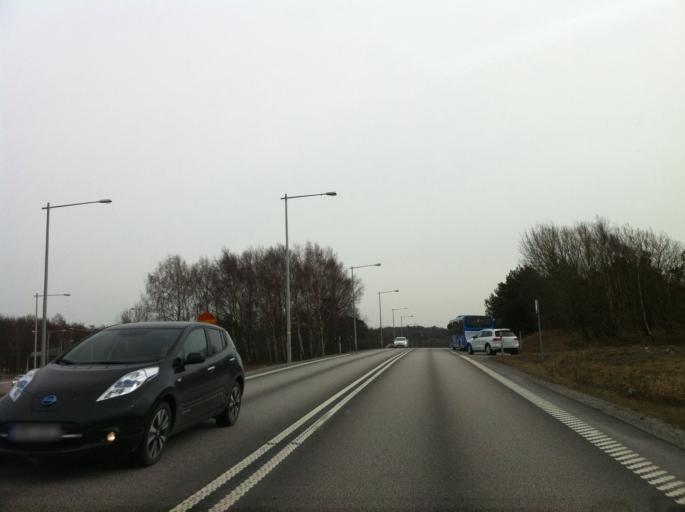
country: SE
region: Vaestra Goetaland
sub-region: Stenungsunds Kommun
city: Stenungsund
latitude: 58.0607
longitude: 11.7941
